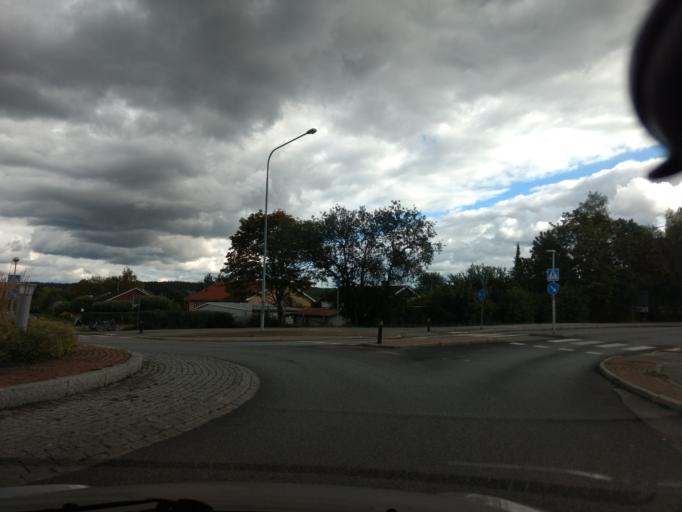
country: SE
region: Uppsala
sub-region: Uppsala Kommun
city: Saevja
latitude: 59.8051
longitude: 17.6525
